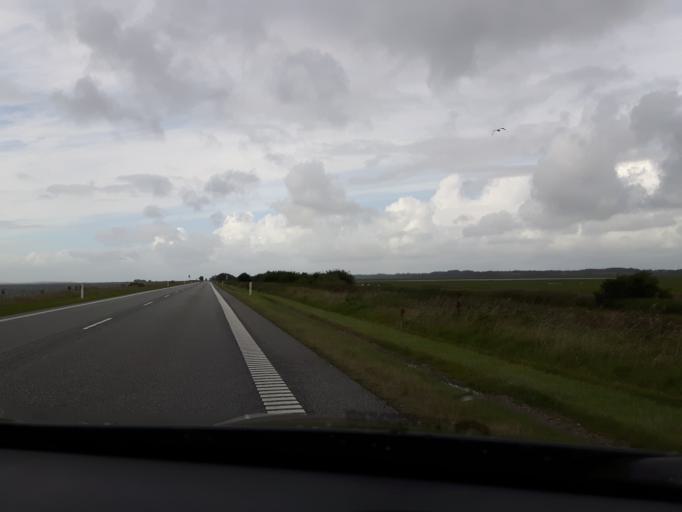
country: DK
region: North Denmark
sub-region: Jammerbugt Kommune
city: Fjerritslev
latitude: 57.0354
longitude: 9.1118
